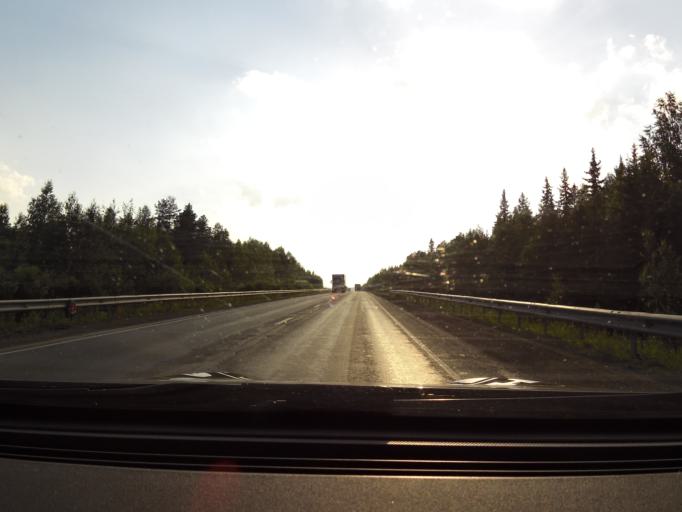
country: RU
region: Sverdlovsk
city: Revda
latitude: 56.8266
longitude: 59.9167
